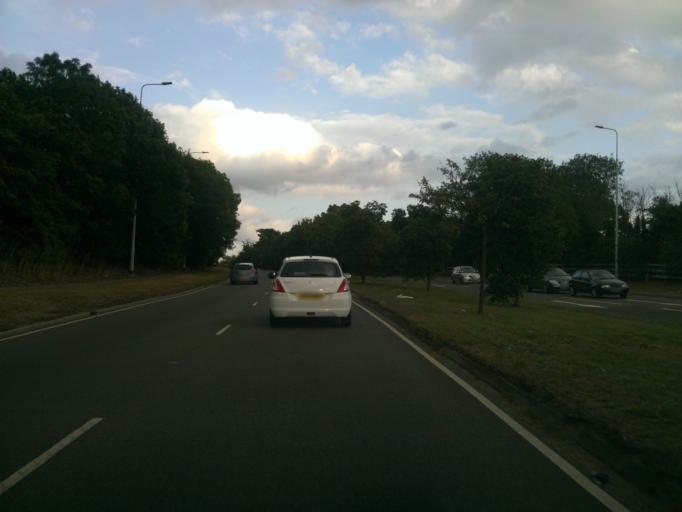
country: GB
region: England
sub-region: Essex
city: Rowhedge
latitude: 51.8814
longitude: 0.9403
